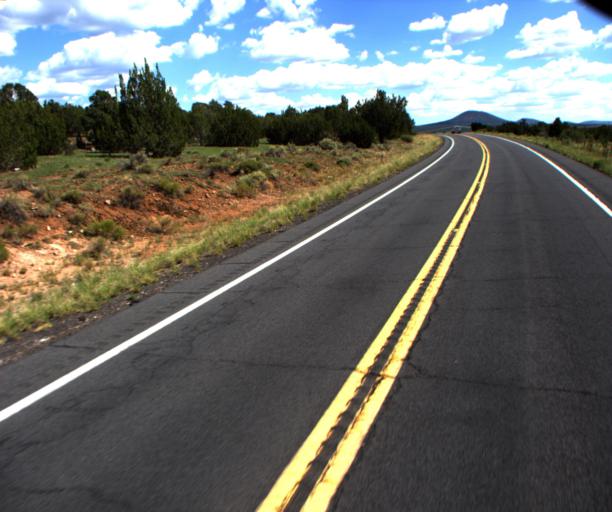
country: US
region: Arizona
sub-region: Coconino County
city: Williams
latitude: 35.4760
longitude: -112.1774
